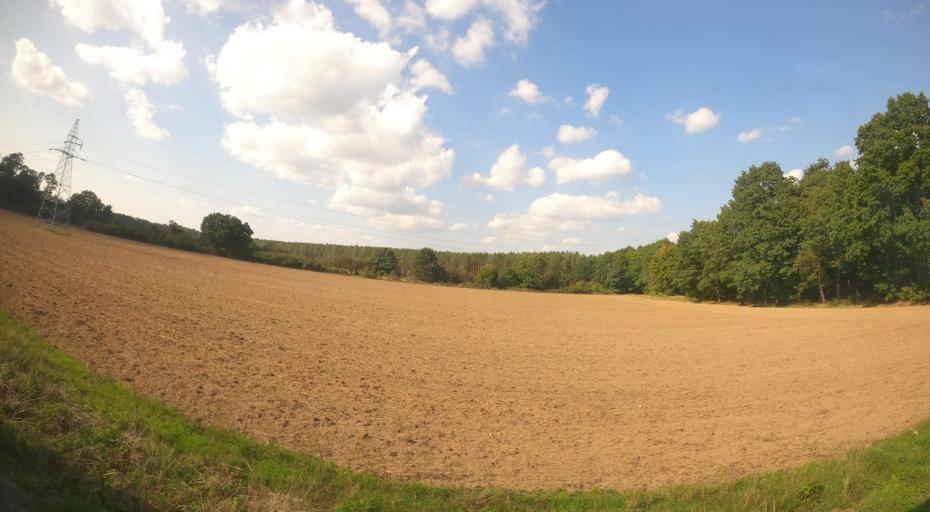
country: PL
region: Lubusz
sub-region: Powiat zielonogorski
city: Swidnica
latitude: 51.9093
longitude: 15.3266
